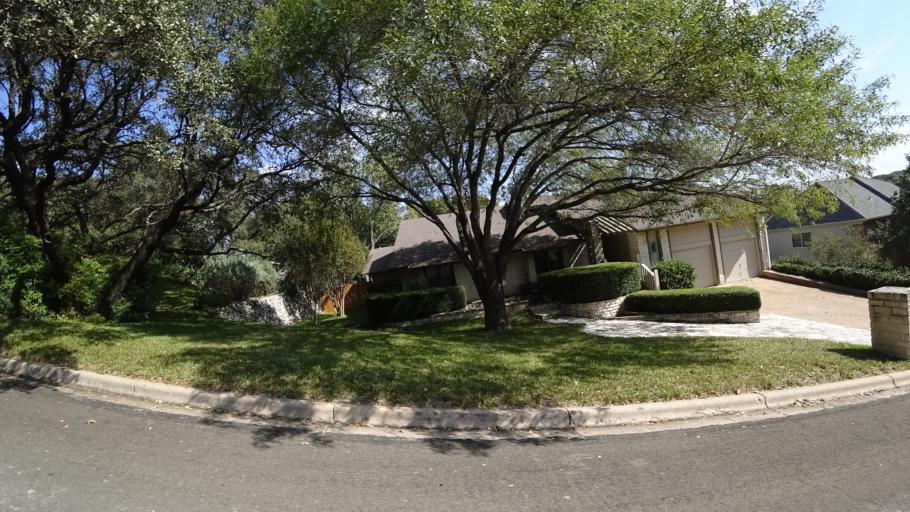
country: US
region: Texas
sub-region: Travis County
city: West Lake Hills
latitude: 30.3453
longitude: -97.7672
